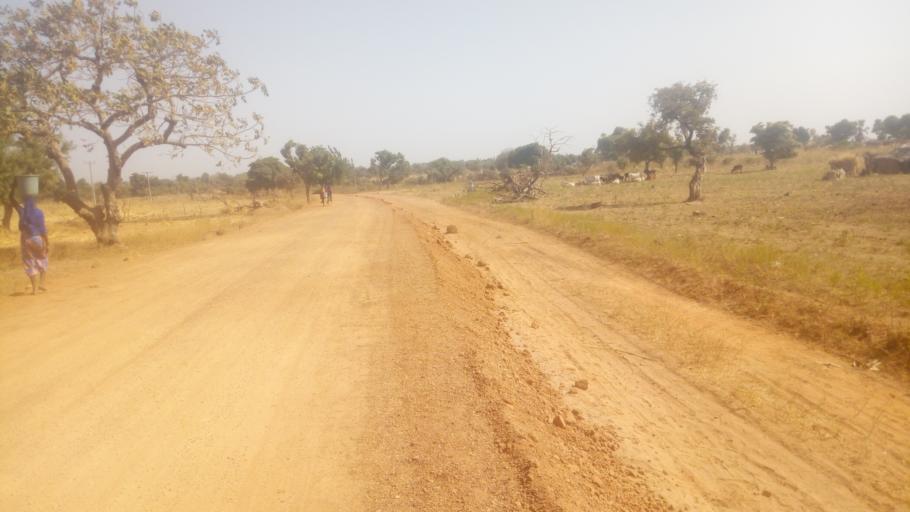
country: NG
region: Adamawa
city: Yola
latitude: 9.2586
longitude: 12.8787
